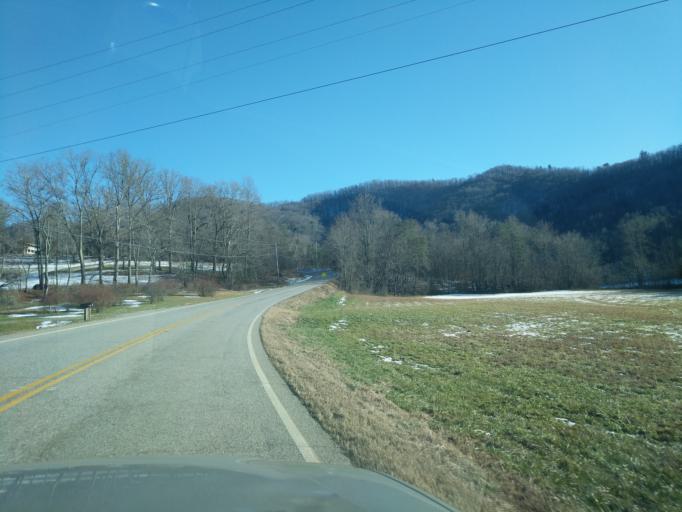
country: US
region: Georgia
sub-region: Towns County
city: Hiawassee
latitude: 34.9258
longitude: -83.6754
